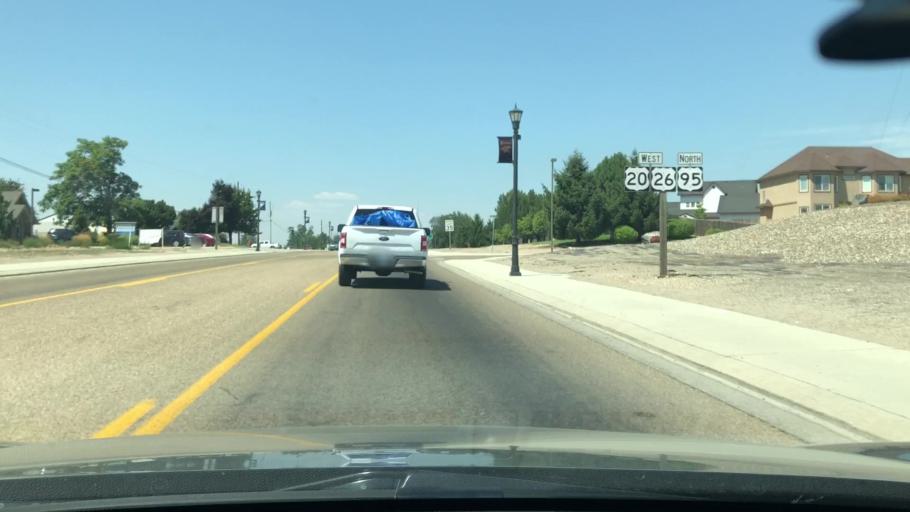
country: US
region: Idaho
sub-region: Canyon County
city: Parma
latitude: 43.7892
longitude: -116.9486
